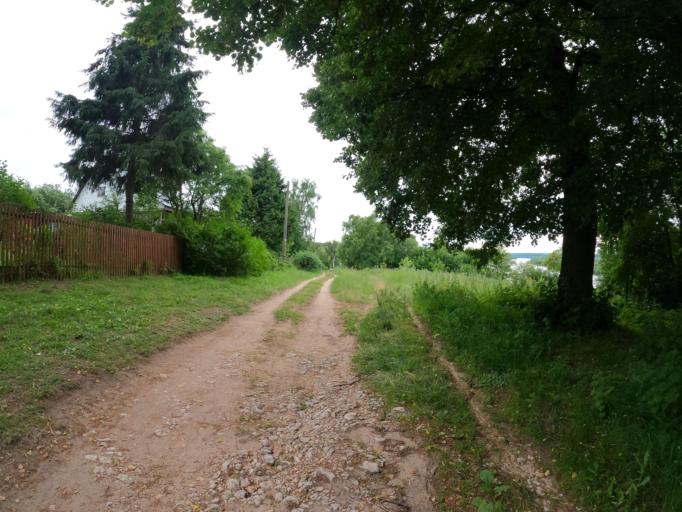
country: RU
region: Moskovskaya
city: Sychevo
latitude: 54.9099
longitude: 38.7317
